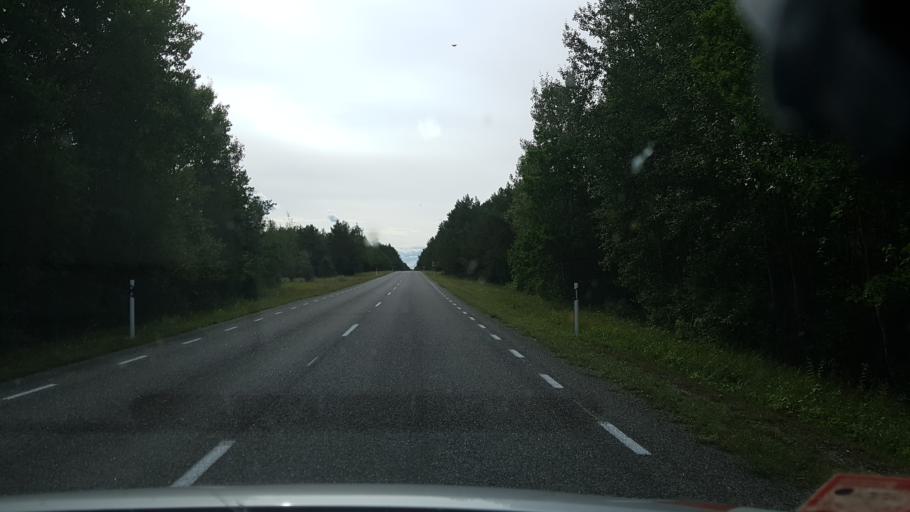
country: EE
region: Saare
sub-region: Kuressaare linn
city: Kuressaare
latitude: 58.4434
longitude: 21.9917
